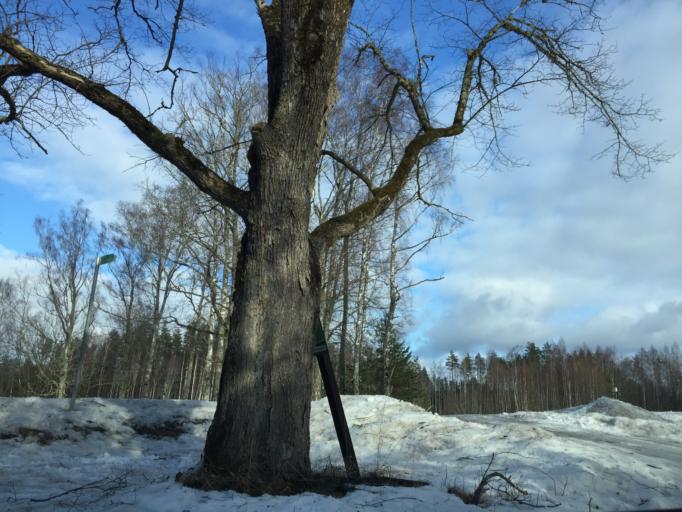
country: LV
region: Salacgrivas
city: Ainazi
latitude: 57.8554
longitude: 24.5181
